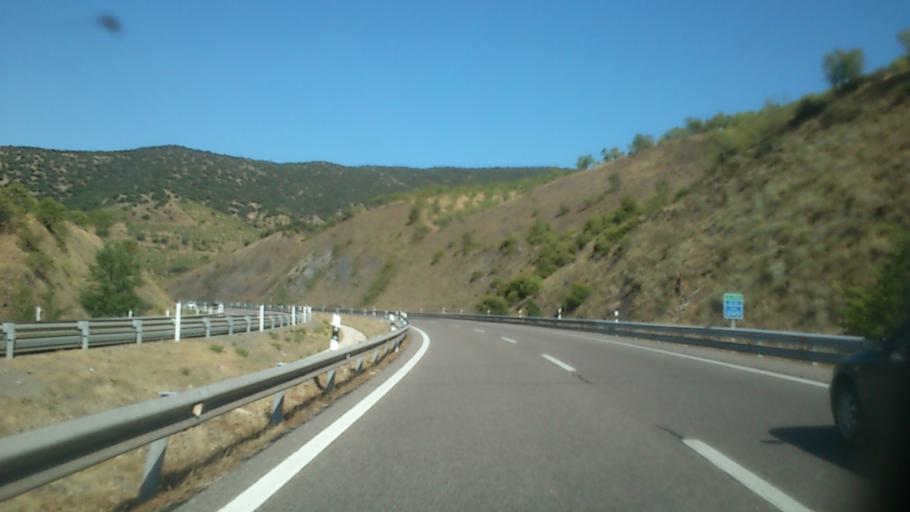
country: ES
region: Aragon
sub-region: Provincia de Zaragoza
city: Paracuellos de la Ribera
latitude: 41.4019
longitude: -1.5331
